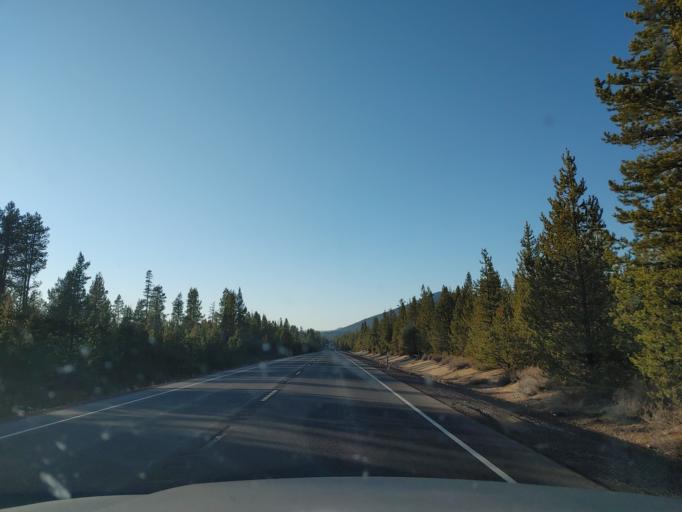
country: US
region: Oregon
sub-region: Deschutes County
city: La Pine
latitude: 43.4009
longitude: -121.8215
